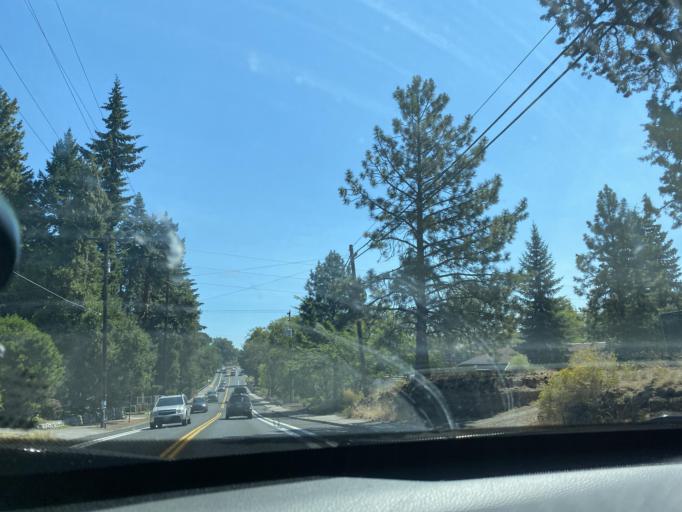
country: US
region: Oregon
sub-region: Deschutes County
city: Bend
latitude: 44.0642
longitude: -121.3129
